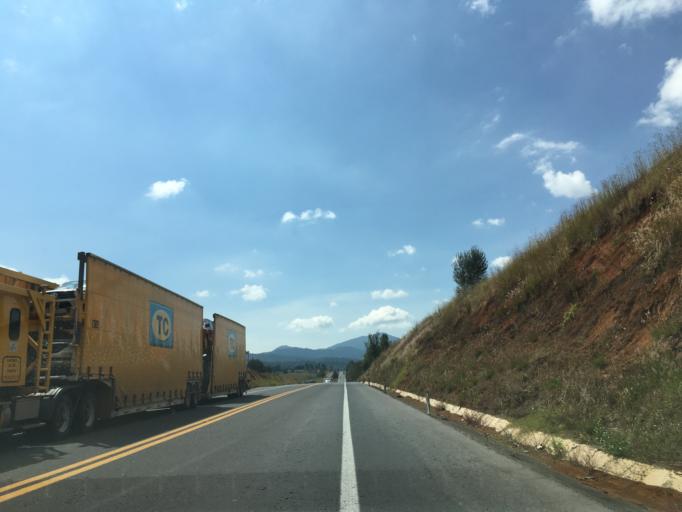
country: MX
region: Michoacan
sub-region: Patzcuaro
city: Colonia Vista Bella (Lomas del Peaje)
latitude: 19.5037
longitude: -101.5803
